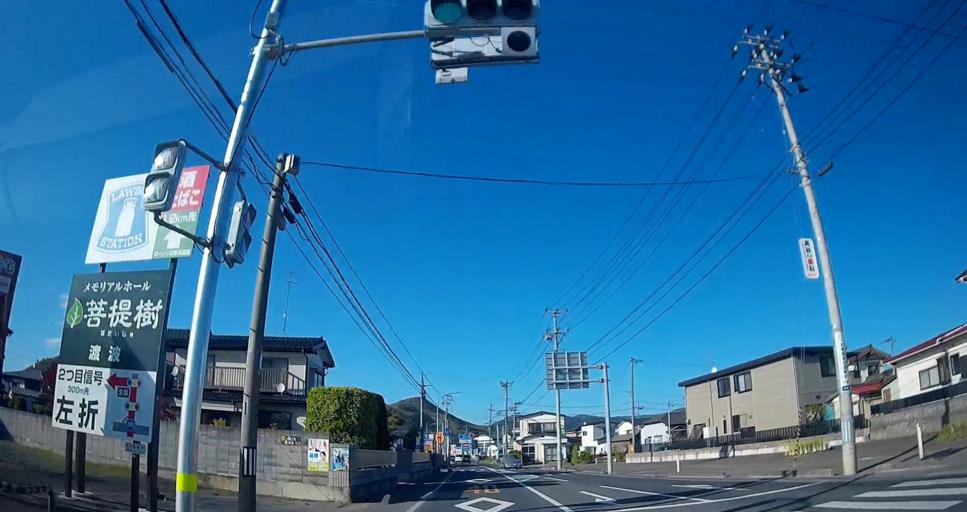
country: JP
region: Miyagi
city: Ishinomaki
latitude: 38.4191
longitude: 141.3666
